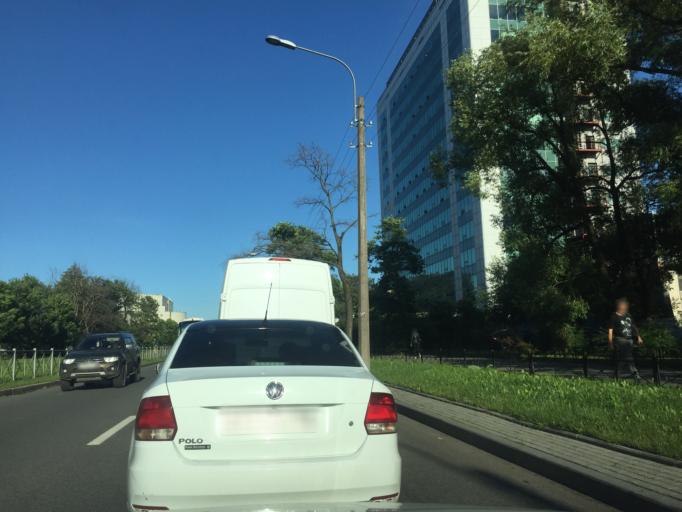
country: RU
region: St.-Petersburg
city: Avtovo
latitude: 59.8647
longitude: 30.3079
